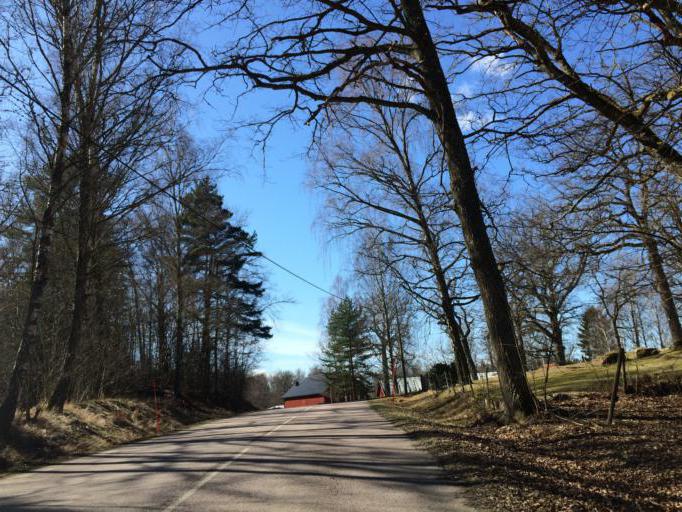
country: SE
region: Vaestmanland
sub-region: Hallstahammars Kommun
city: Kolback
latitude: 59.5200
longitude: 16.3036
